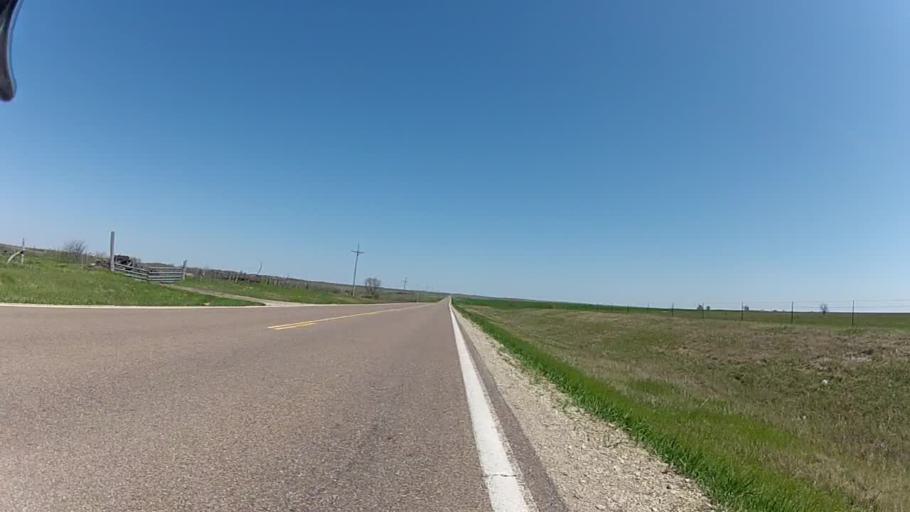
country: US
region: Kansas
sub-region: Morris County
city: Council Grove
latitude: 38.8921
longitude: -96.5202
